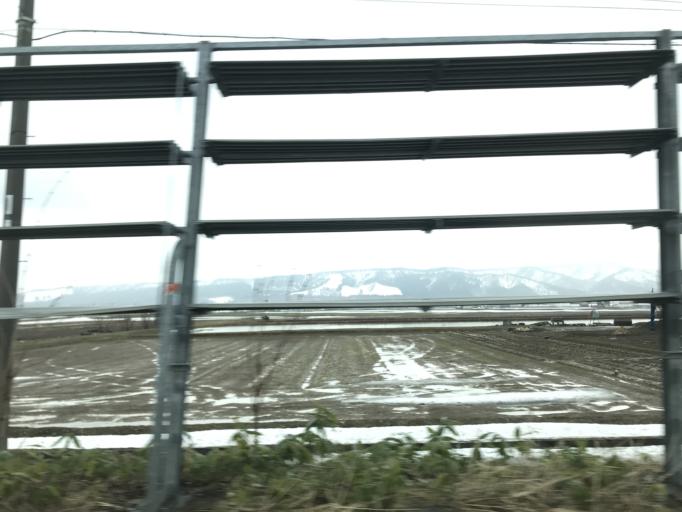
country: JP
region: Hokkaido
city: Nayoro
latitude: 44.2274
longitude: 142.3948
